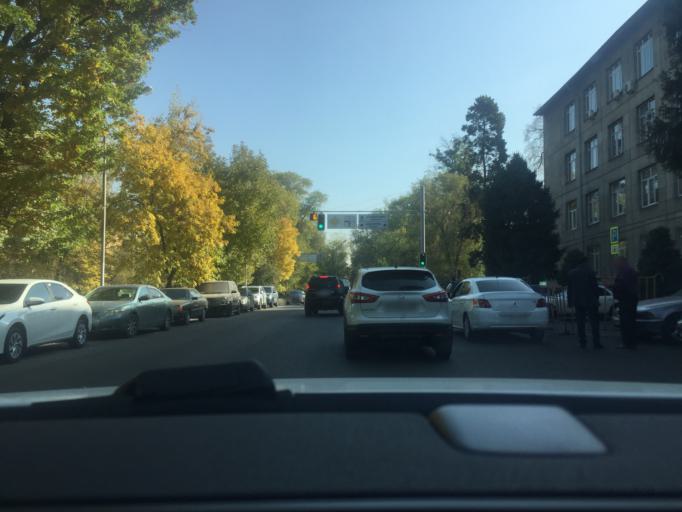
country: KZ
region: Almaty Qalasy
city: Almaty
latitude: 43.2502
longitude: 76.9288
